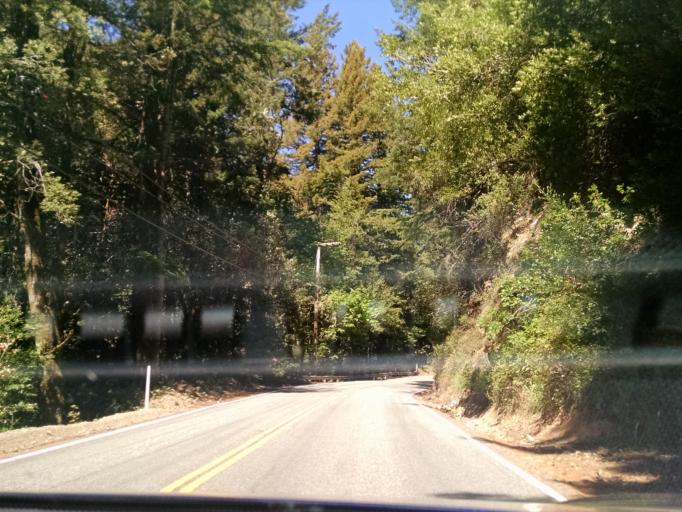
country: US
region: California
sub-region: San Mateo County
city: Woodside
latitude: 37.3931
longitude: -122.2915
